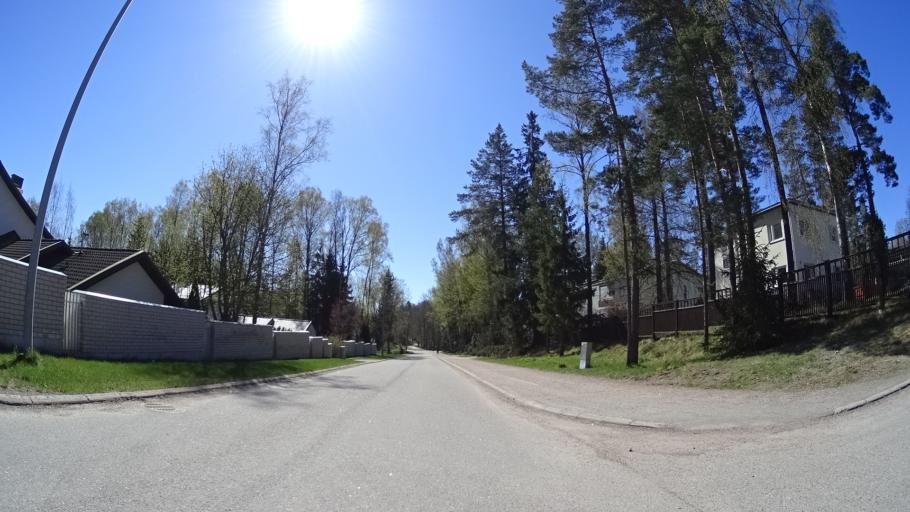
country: FI
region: Uusimaa
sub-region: Helsinki
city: Koukkuniemi
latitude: 60.1667
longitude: 24.7879
